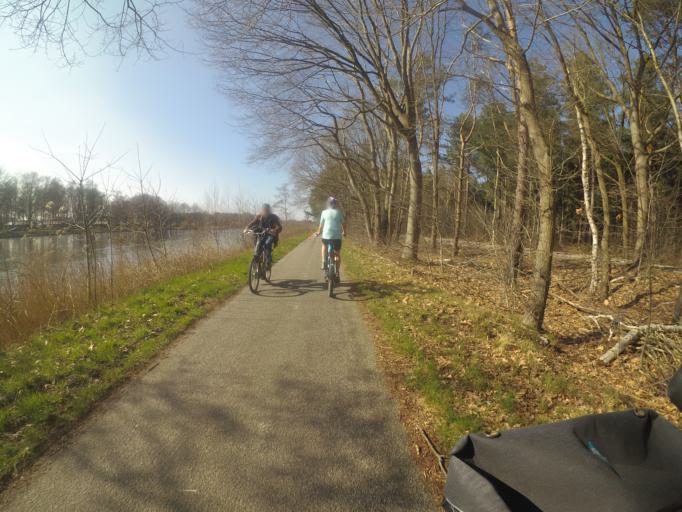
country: NL
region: North Brabant
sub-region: Gemeente Hilvarenbeek
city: Hilvarenbeek
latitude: 51.5273
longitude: 5.1353
